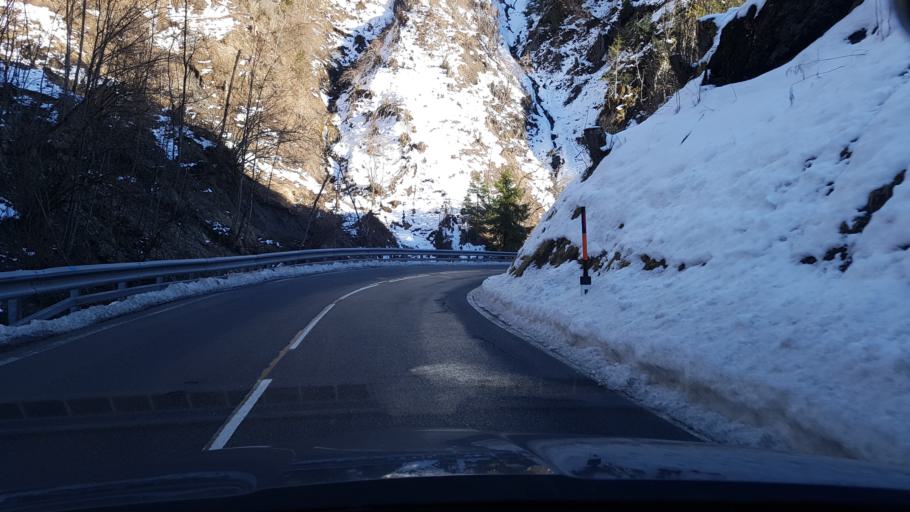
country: AT
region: Salzburg
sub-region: Politischer Bezirk Zell am See
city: Lend
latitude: 47.3102
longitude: 13.0329
